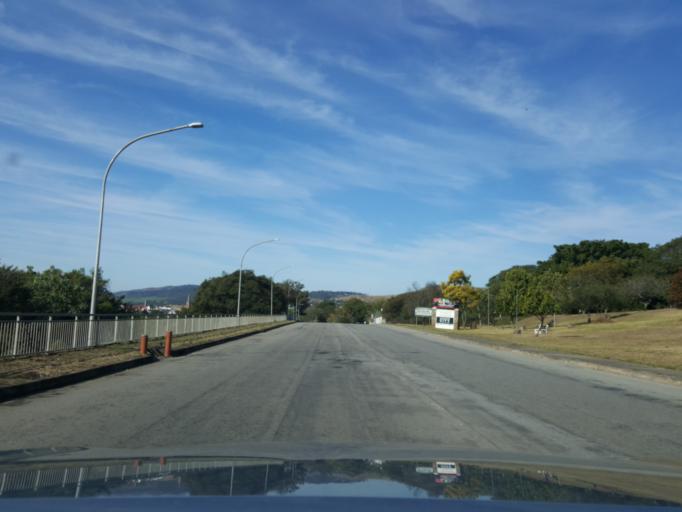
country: ZA
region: Eastern Cape
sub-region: Cacadu District Municipality
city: Grahamstown
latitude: -33.3044
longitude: 26.5084
